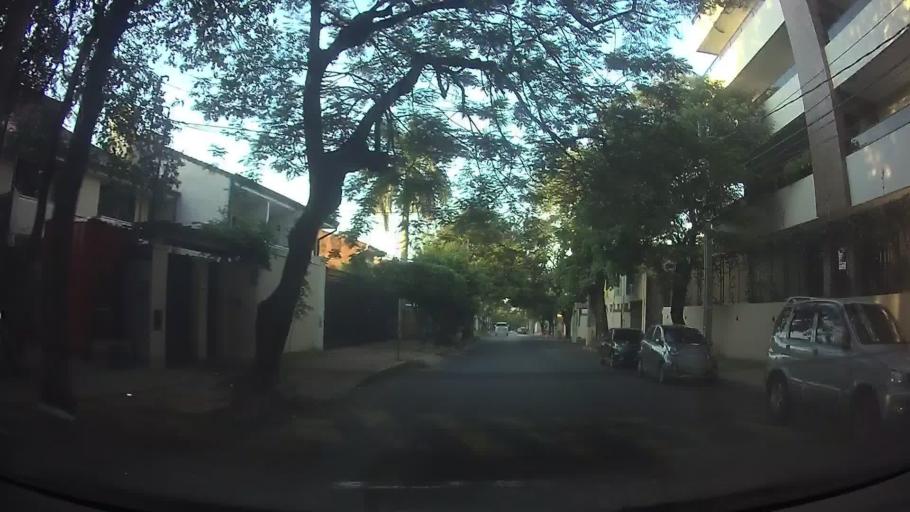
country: PY
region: Central
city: Lambare
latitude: -25.3080
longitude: -57.5779
